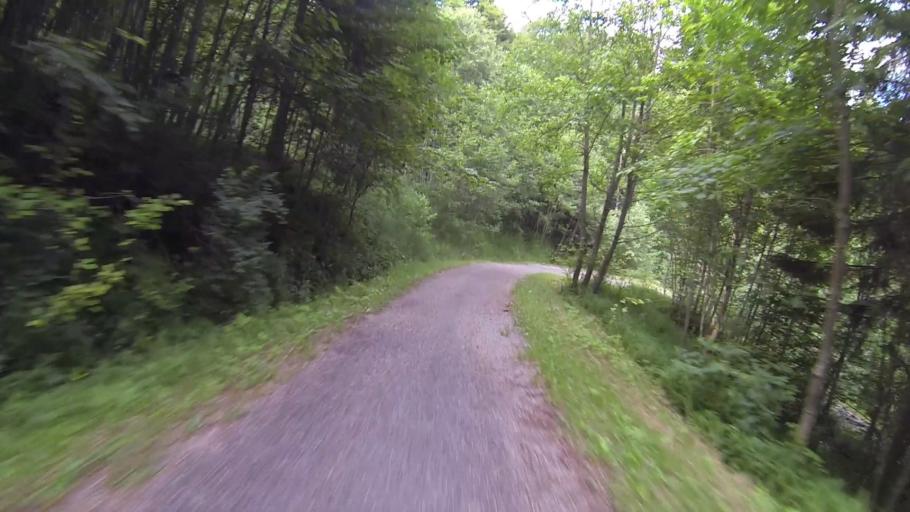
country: AT
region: Tyrol
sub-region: Politischer Bezirk Reutte
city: Jungholz
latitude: 47.5714
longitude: 10.4720
